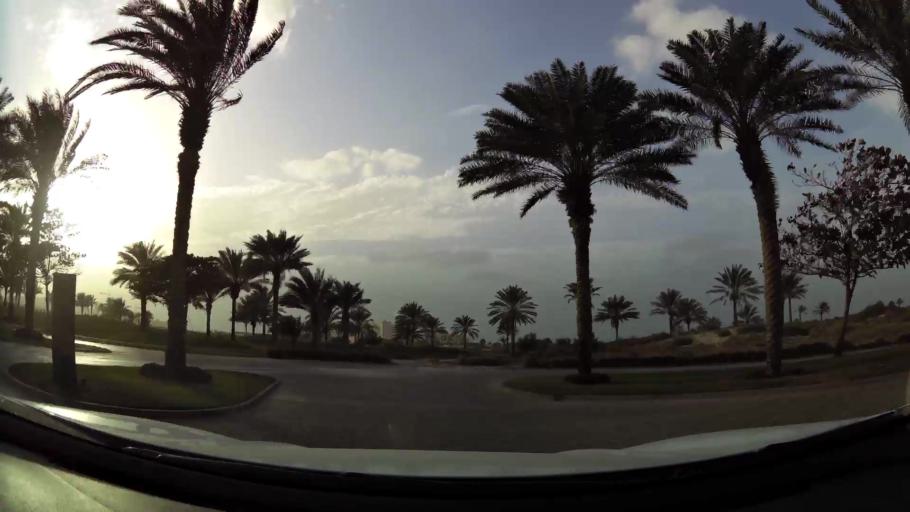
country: AE
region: Abu Dhabi
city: Abu Dhabi
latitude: 24.5438
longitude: 54.4399
